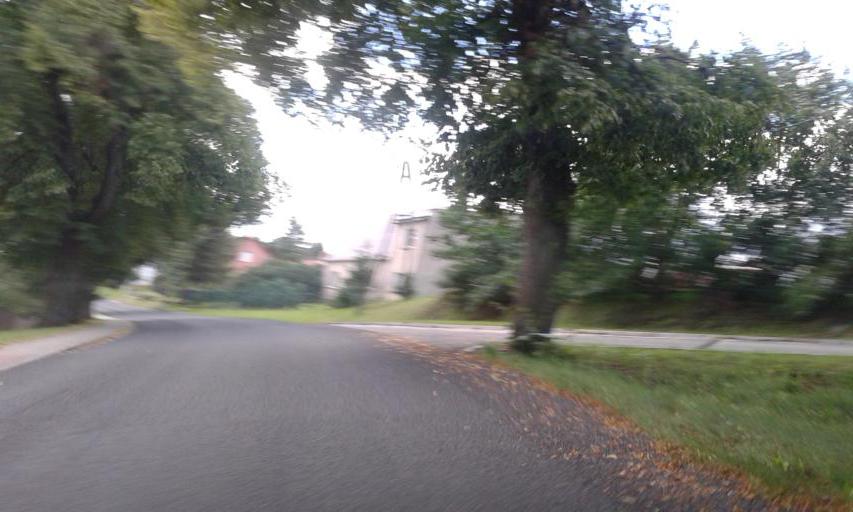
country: PL
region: West Pomeranian Voivodeship
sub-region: Powiat walecki
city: Walcz
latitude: 53.2352
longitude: 16.5382
